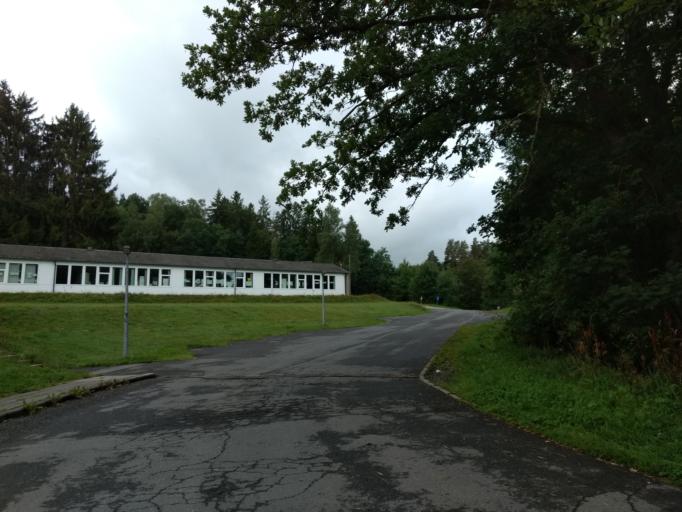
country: BE
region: Wallonia
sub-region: Province du Luxembourg
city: Houffalize
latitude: 50.1292
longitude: 5.7819
